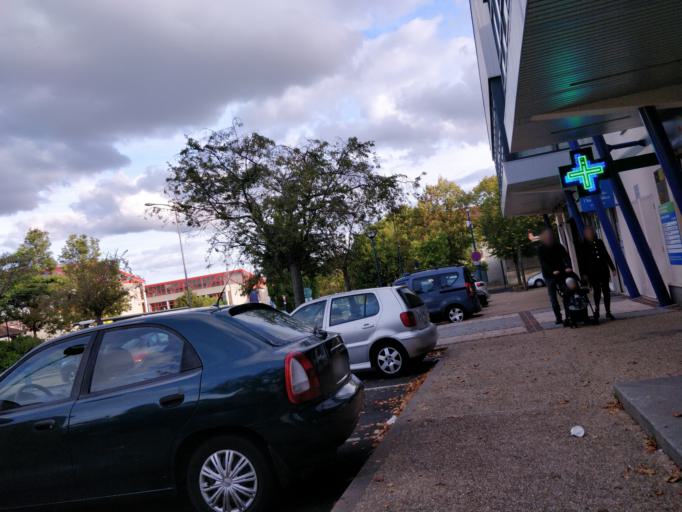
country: FR
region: Ile-de-France
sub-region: Departement du Val-d'Oise
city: Vaureal
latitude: 49.0330
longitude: 2.0198
